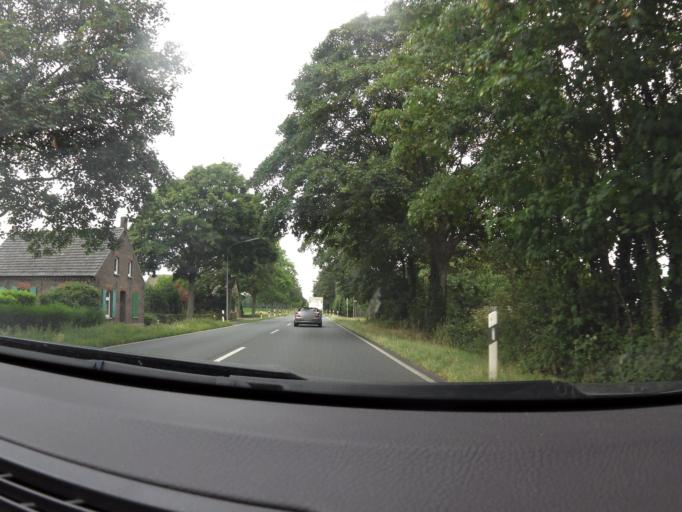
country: DE
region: North Rhine-Westphalia
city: Straelen
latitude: 51.4654
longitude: 6.2816
